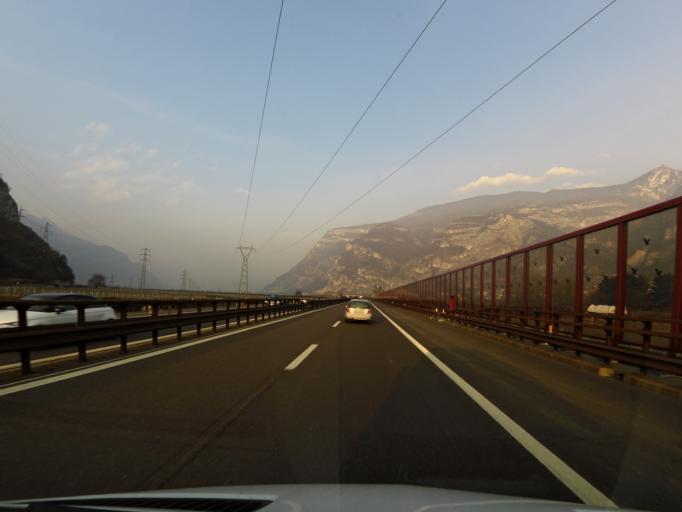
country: IT
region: Trentino-Alto Adige
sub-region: Provincia di Trento
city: Calliano
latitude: 45.9416
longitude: 11.0951
